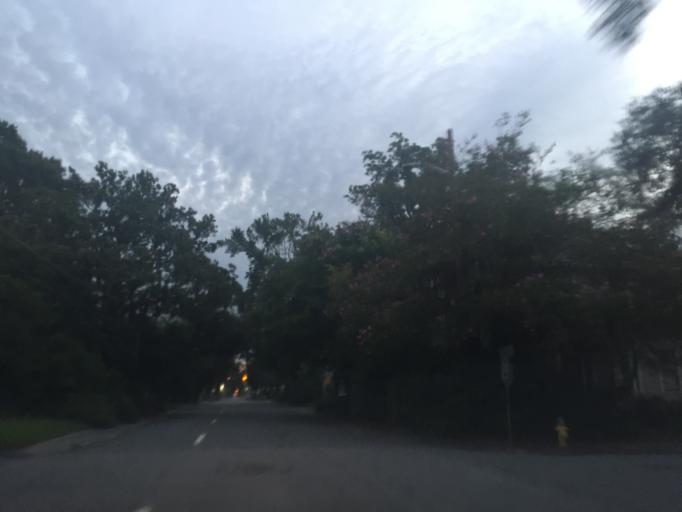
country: US
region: Georgia
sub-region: Chatham County
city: Savannah
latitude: 32.0516
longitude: -81.0941
